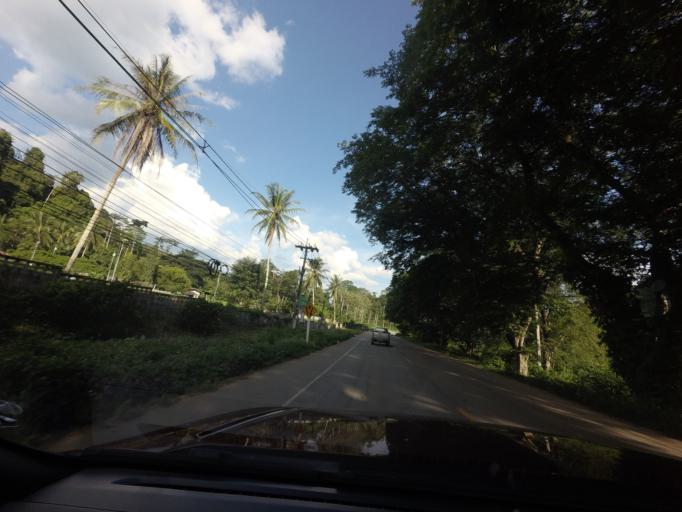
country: TH
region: Yala
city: Than To
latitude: 6.1739
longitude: 101.1776
